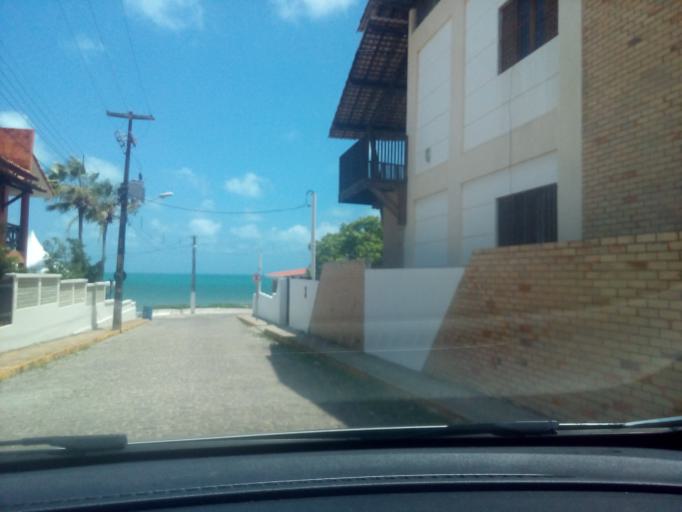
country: BR
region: Rio Grande do Norte
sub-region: Parnamirim
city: Parnamirim
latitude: -5.9679
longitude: -35.1303
